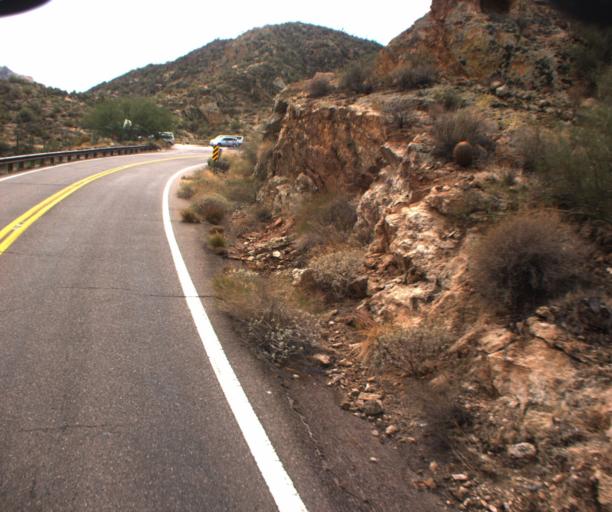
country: US
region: Arizona
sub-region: Pinal County
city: Apache Junction
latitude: 33.5420
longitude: -111.4493
